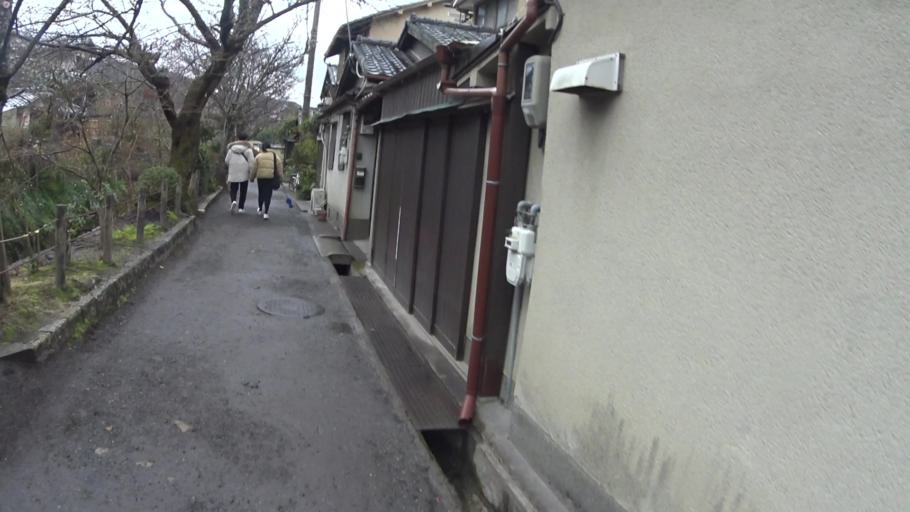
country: JP
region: Kyoto
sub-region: Kyoto-shi
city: Kamigyo-ku
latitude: 35.0201
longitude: 135.7939
